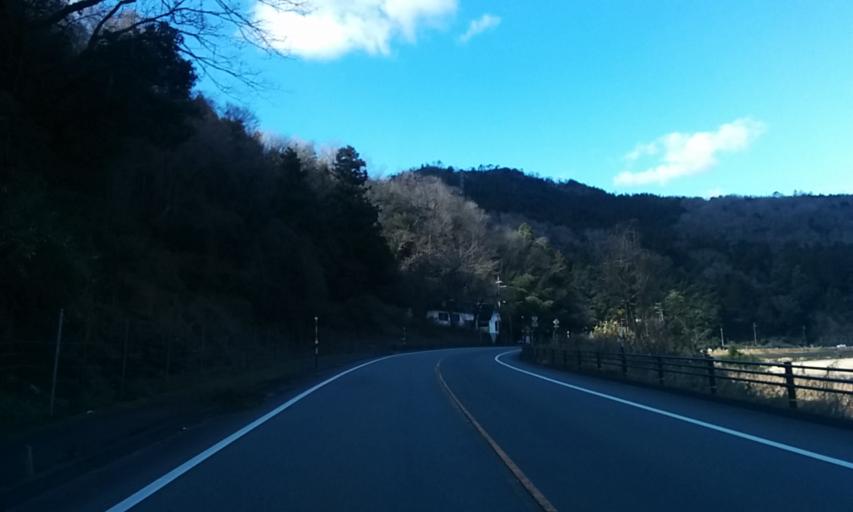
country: JP
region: Hyogo
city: Toyooka
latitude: 35.4596
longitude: 134.9254
